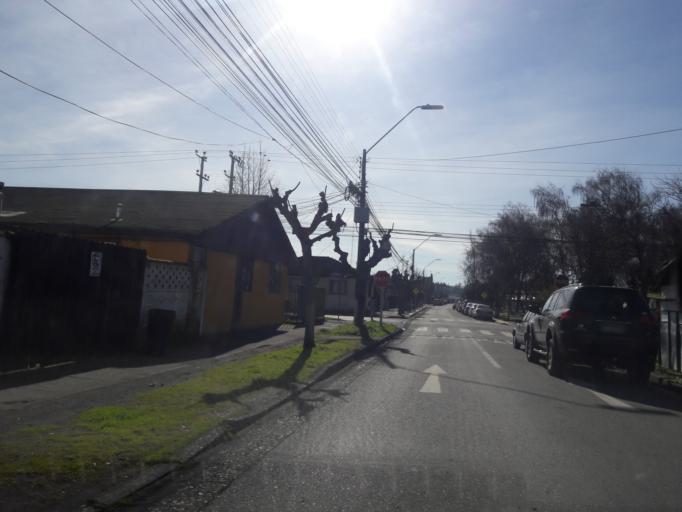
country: CL
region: Biobio
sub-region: Provincia de Biobio
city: Cabrero
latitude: -37.0366
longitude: -72.4033
